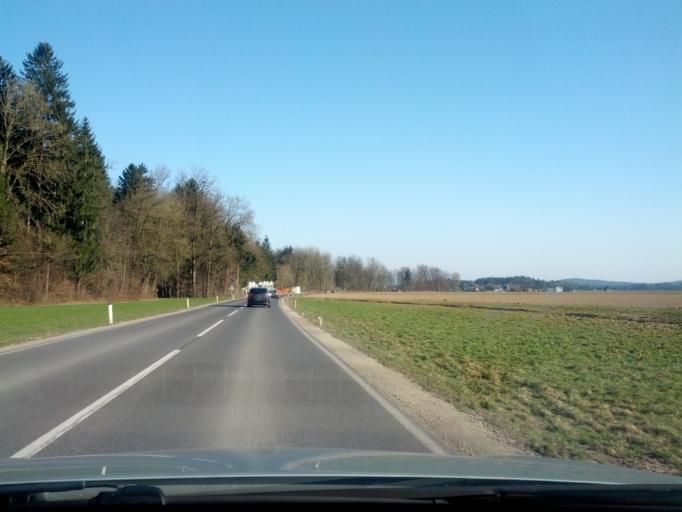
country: SI
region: Cerklje na Gorenjskem
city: Cerklje na Gorenjskem
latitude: 46.2245
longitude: 14.4928
